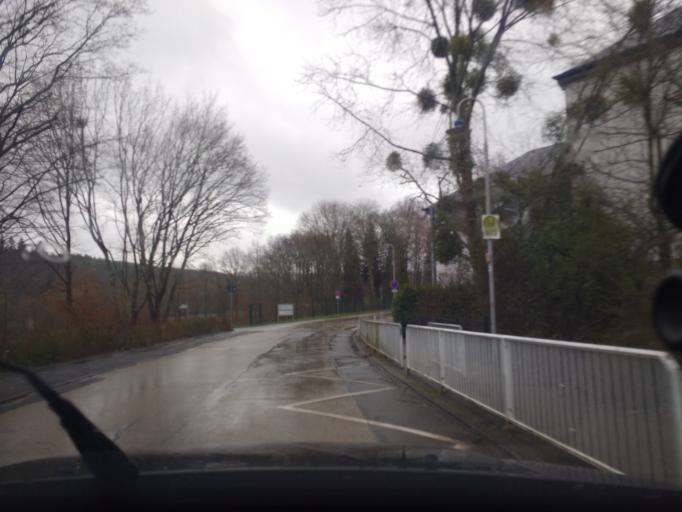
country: DE
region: Rheinland-Pfalz
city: Konz
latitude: 49.6930
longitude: 6.5857
